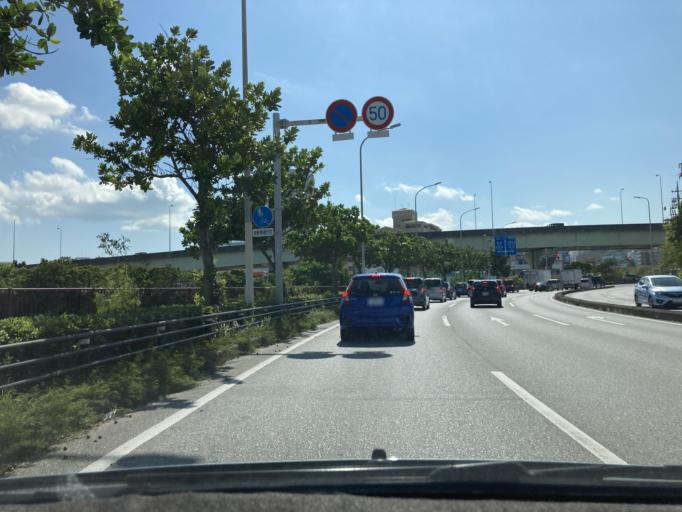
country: JP
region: Okinawa
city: Ginowan
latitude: 26.2684
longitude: 127.7268
